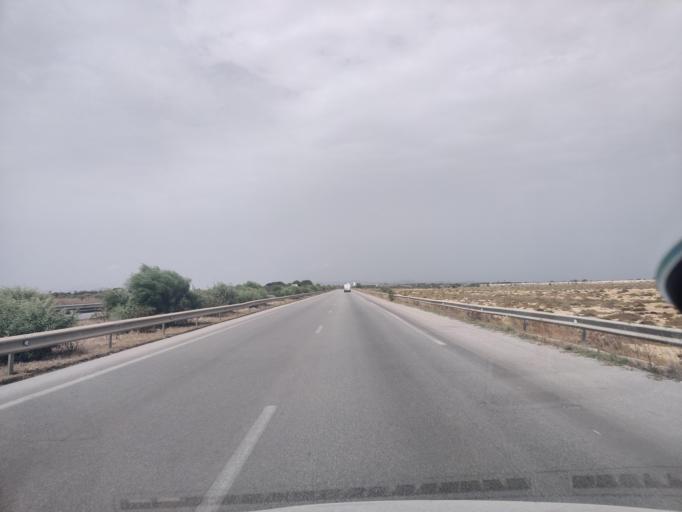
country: TN
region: Susah
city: Harqalah
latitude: 36.0724
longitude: 10.4050
